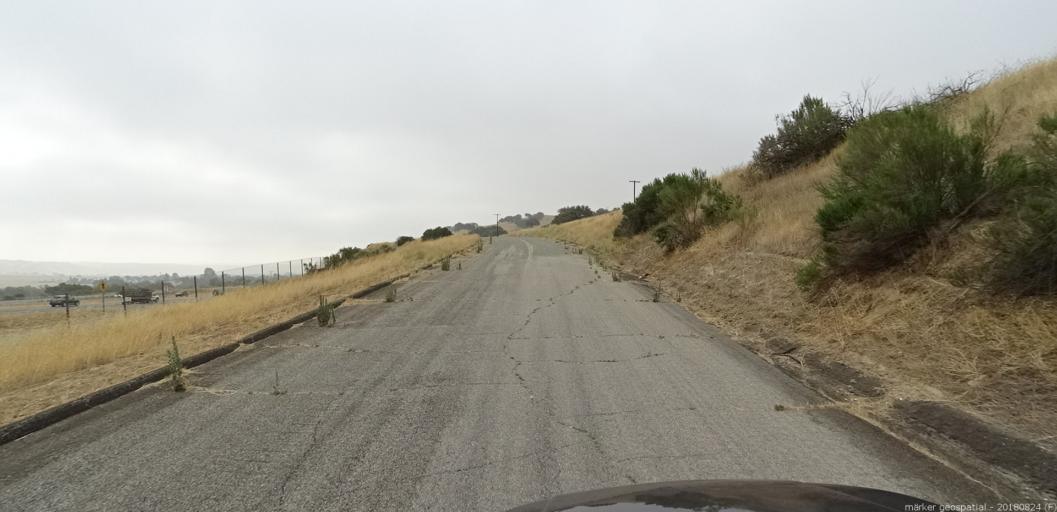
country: US
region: California
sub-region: San Luis Obispo County
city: Lake Nacimiento
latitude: 35.8639
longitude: -120.8178
